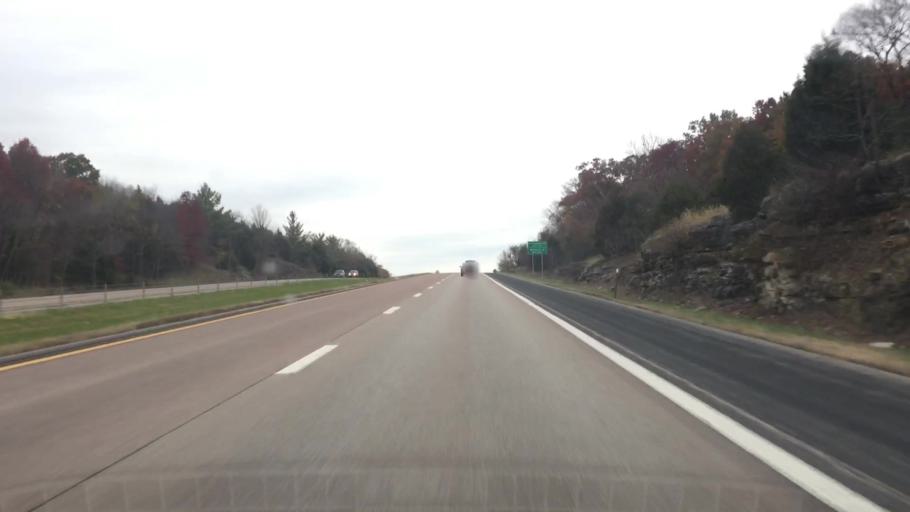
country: US
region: Missouri
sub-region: Boone County
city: Ashland
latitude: 38.6913
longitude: -92.2549
